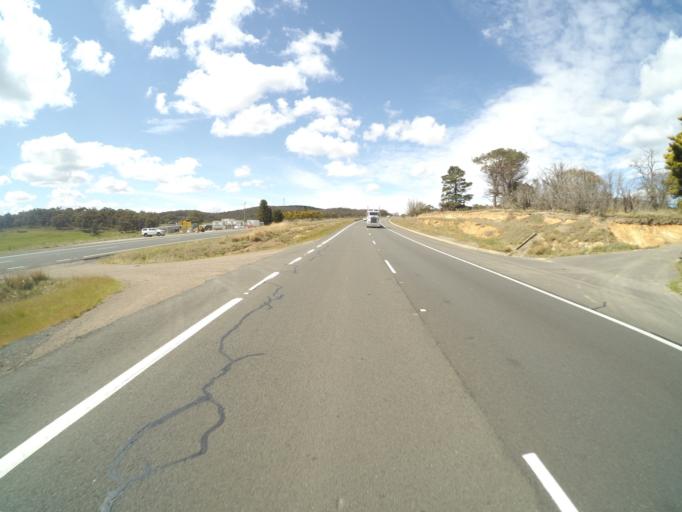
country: AU
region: New South Wales
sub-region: Goulburn Mulwaree
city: Goulburn
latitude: -34.7415
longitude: 149.9125
